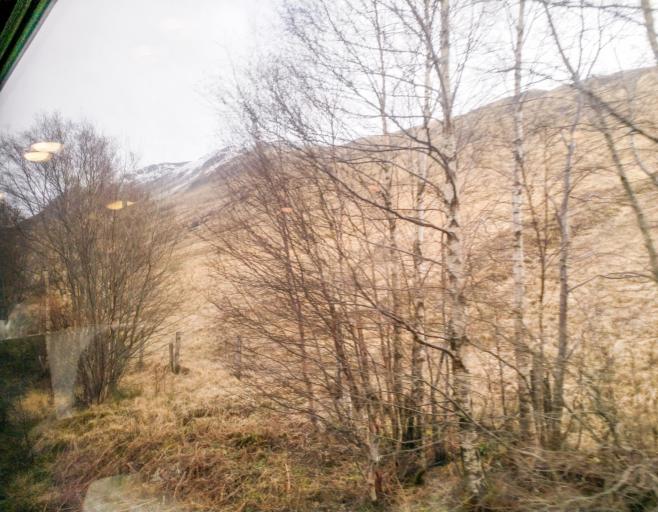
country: GB
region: Scotland
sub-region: Highland
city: Spean Bridge
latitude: 56.8145
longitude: -4.7152
